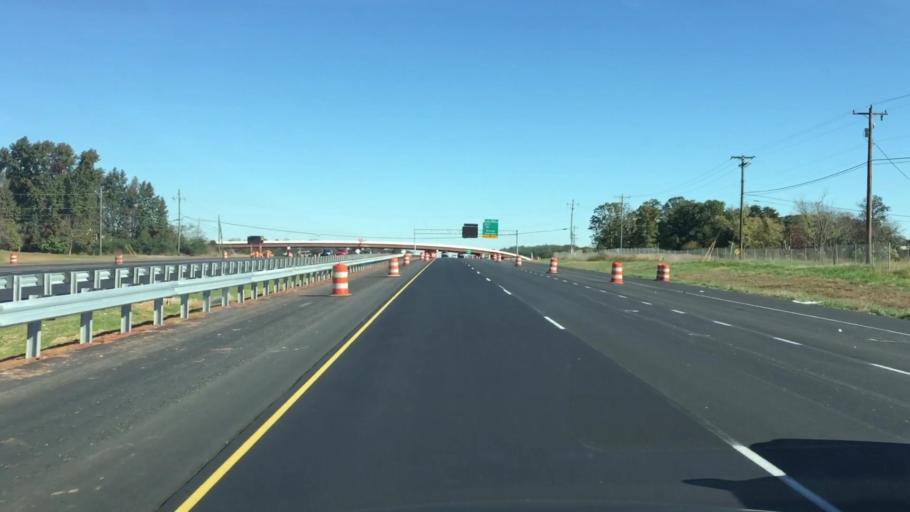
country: US
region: North Carolina
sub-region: Guilford County
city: Greensboro
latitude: 36.1379
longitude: -79.7390
